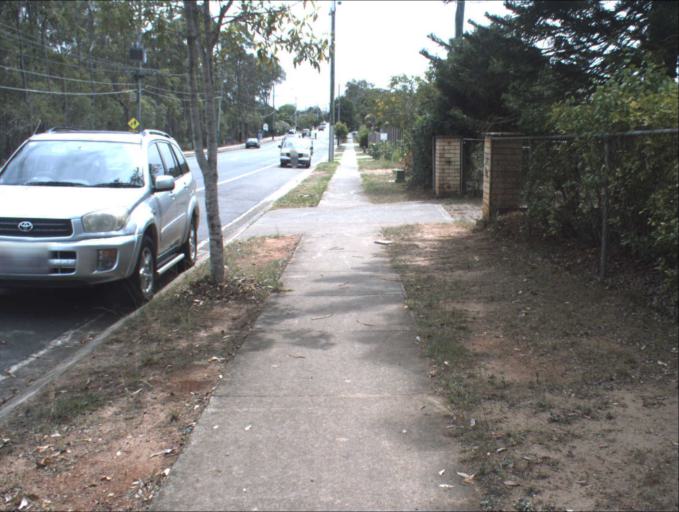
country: AU
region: Queensland
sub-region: Logan
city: Slacks Creek
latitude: -27.6511
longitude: 153.1688
